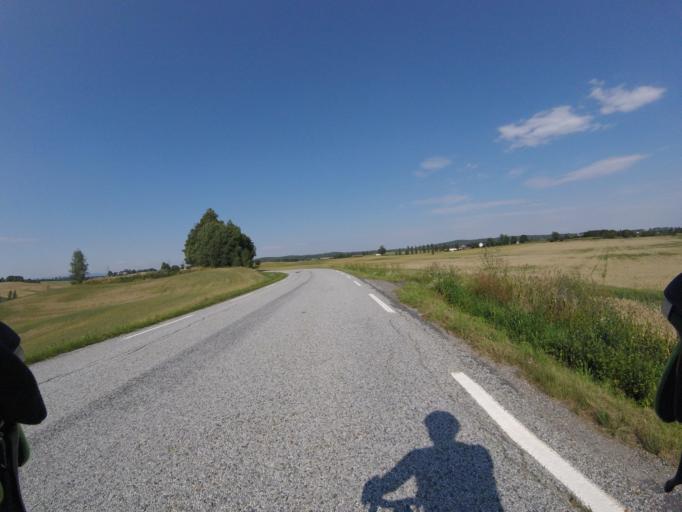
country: NO
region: Akershus
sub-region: Ullensaker
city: Klofta
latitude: 60.0919
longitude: 11.1607
